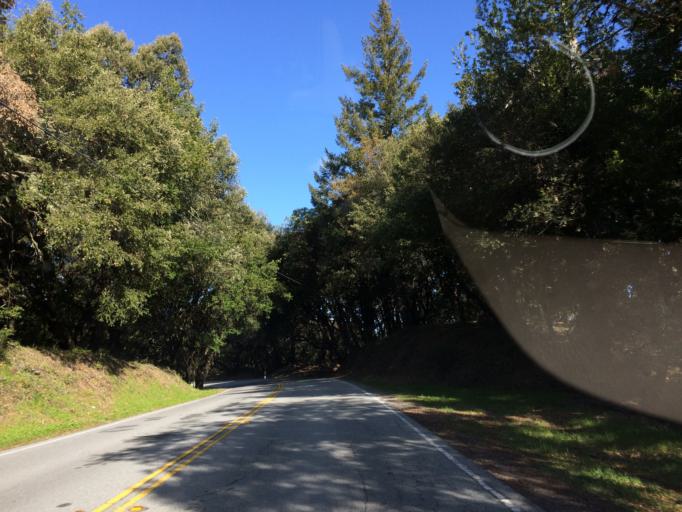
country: US
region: California
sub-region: Santa Clara County
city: Loyola
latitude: 37.2650
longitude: -122.1353
